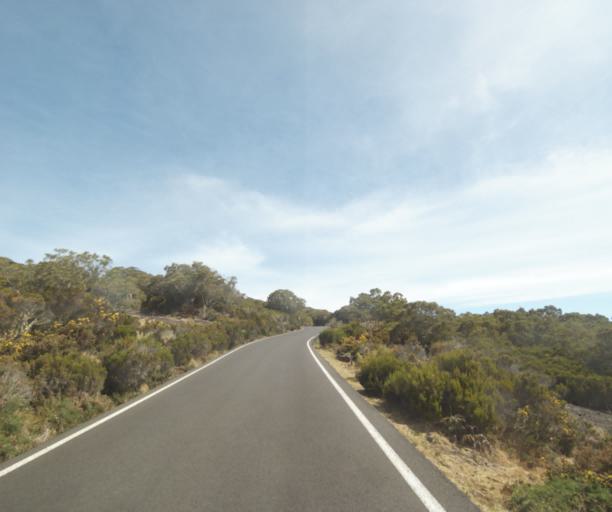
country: RE
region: Reunion
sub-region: Reunion
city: Trois-Bassins
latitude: -21.0634
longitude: 55.3785
